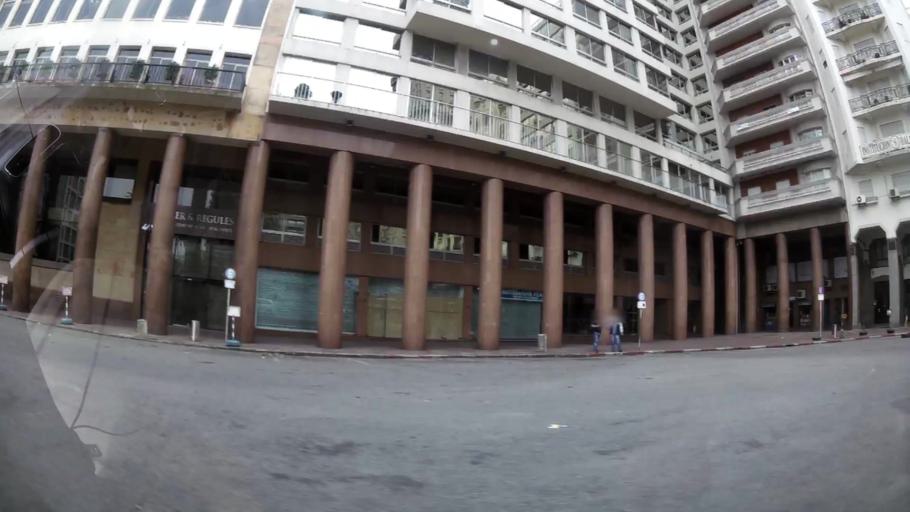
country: UY
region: Montevideo
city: Montevideo
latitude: -34.9064
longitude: -56.1988
